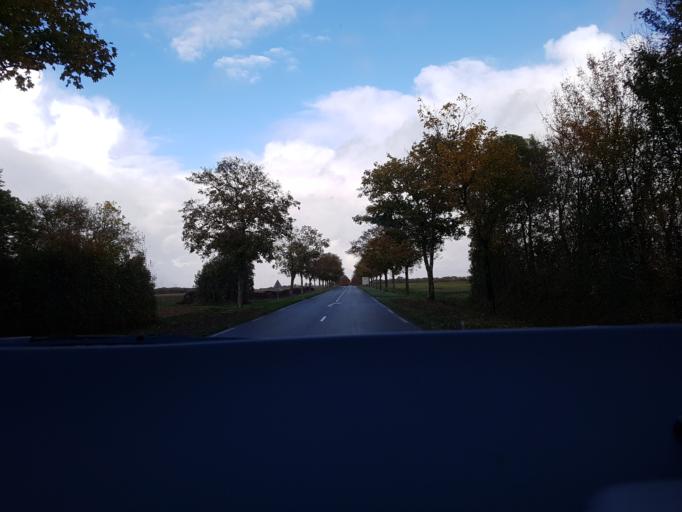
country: FR
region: Poitou-Charentes
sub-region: Departement des Deux-Sevres
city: Brioux-sur-Boutonne
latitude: 46.0893
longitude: -0.2890
